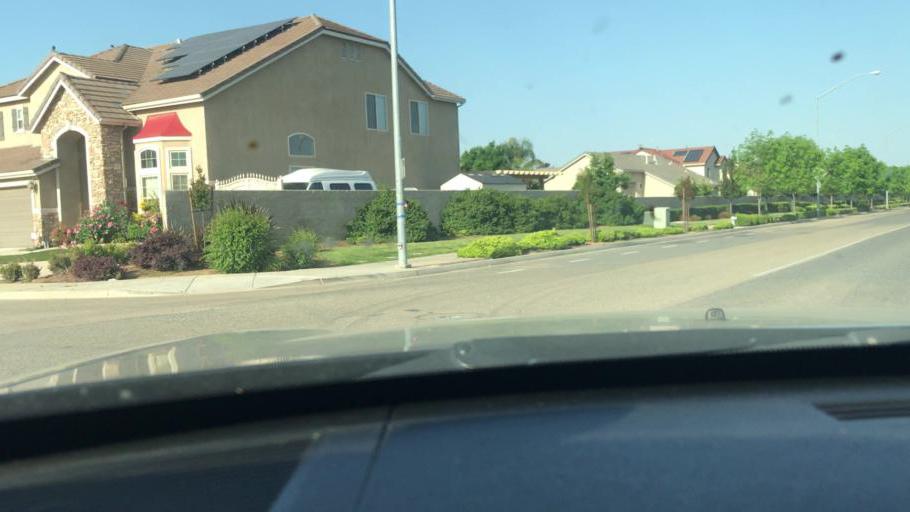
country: US
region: California
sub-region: Fresno County
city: Tarpey Village
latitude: 36.7791
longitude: -119.6679
